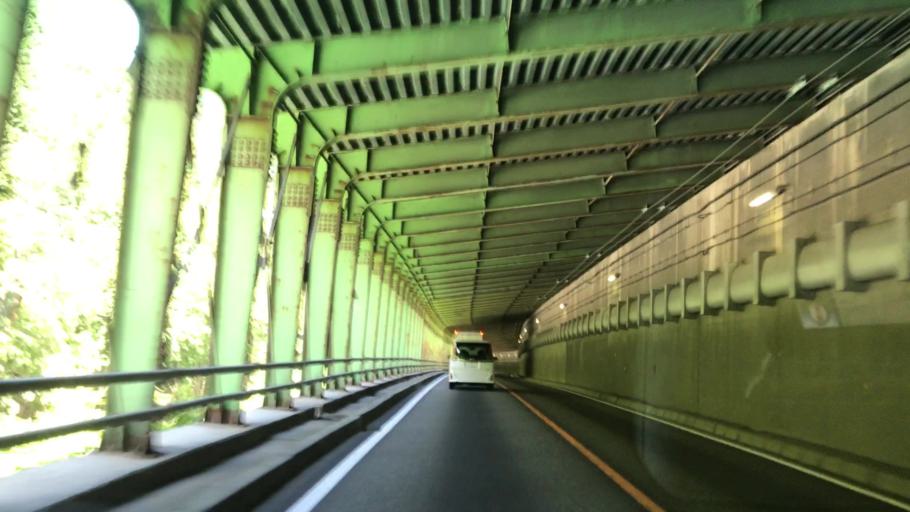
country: JP
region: Hokkaido
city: Shimo-furano
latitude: 42.9399
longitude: 142.6022
